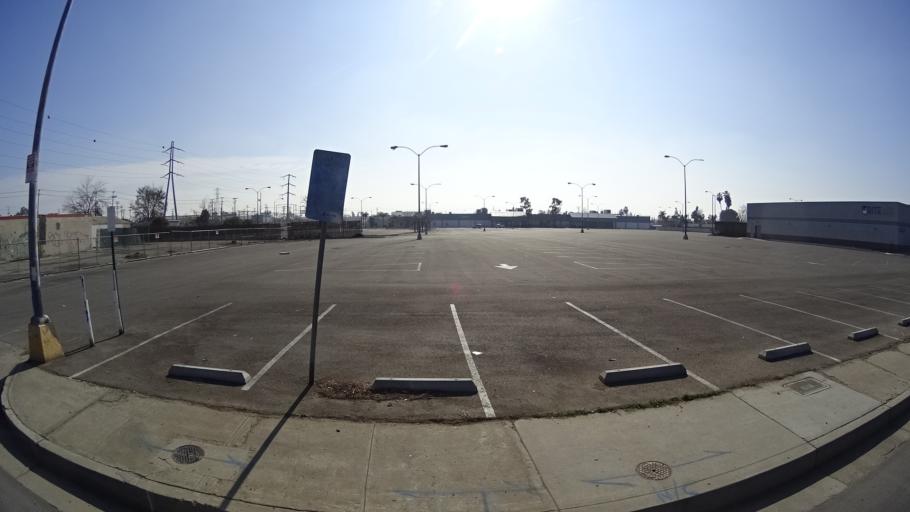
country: US
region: California
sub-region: Kern County
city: Bakersfield
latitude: 35.3904
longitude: -119.0060
